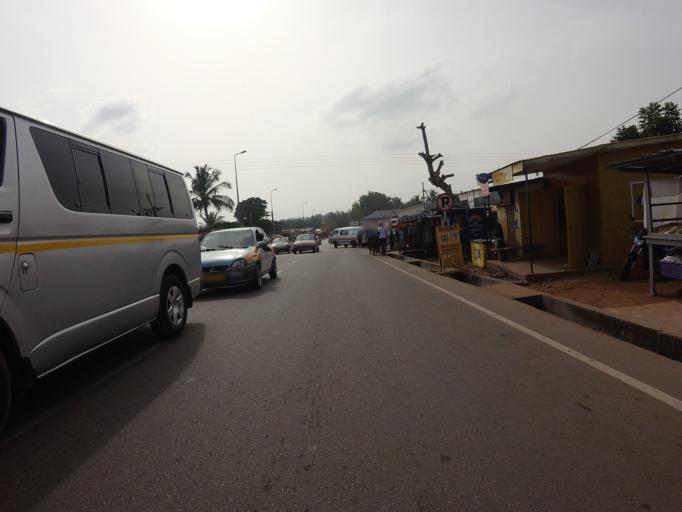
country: GH
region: Volta
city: Ho
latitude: 6.6150
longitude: 0.4741
